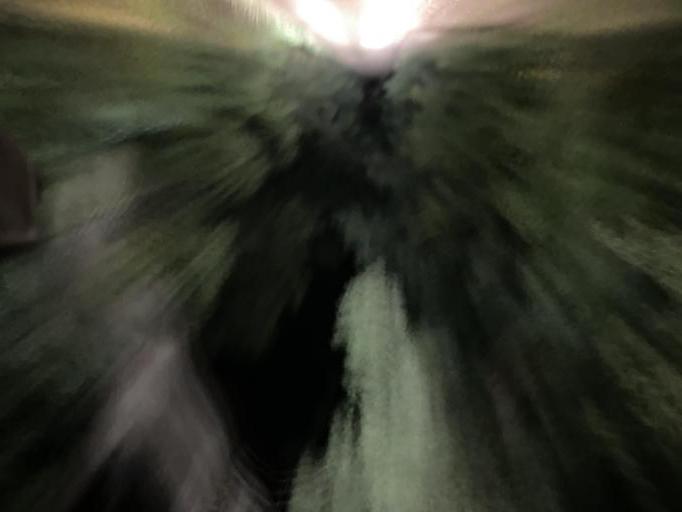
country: FR
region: Auvergne
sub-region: Departement du Puy-de-Dome
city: Courpiere
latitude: 45.7668
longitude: 3.4833
